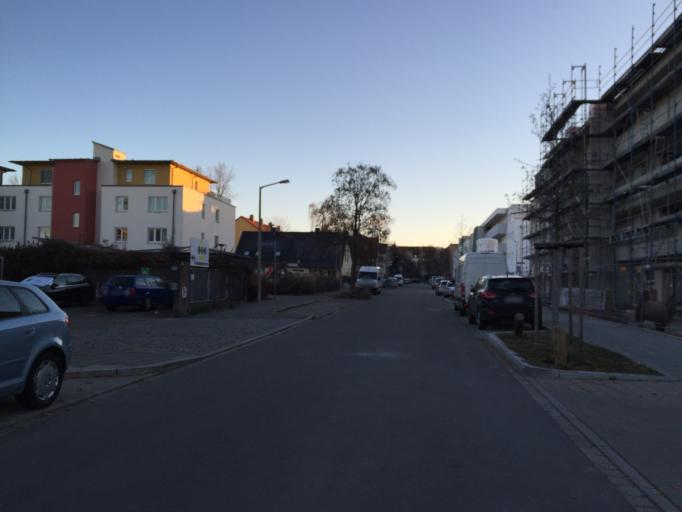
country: DE
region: Bavaria
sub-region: Regierungsbezirk Mittelfranken
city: Nuernberg
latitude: 49.4674
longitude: 11.0785
